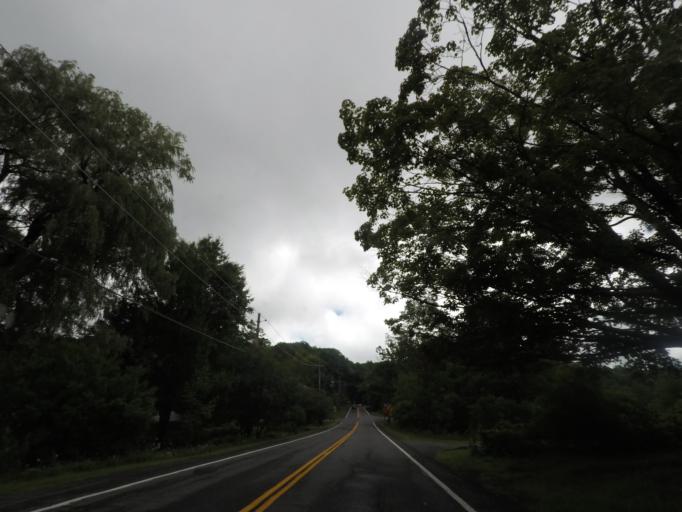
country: US
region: New York
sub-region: Rensselaer County
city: Averill Park
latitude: 42.5800
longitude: -73.4737
